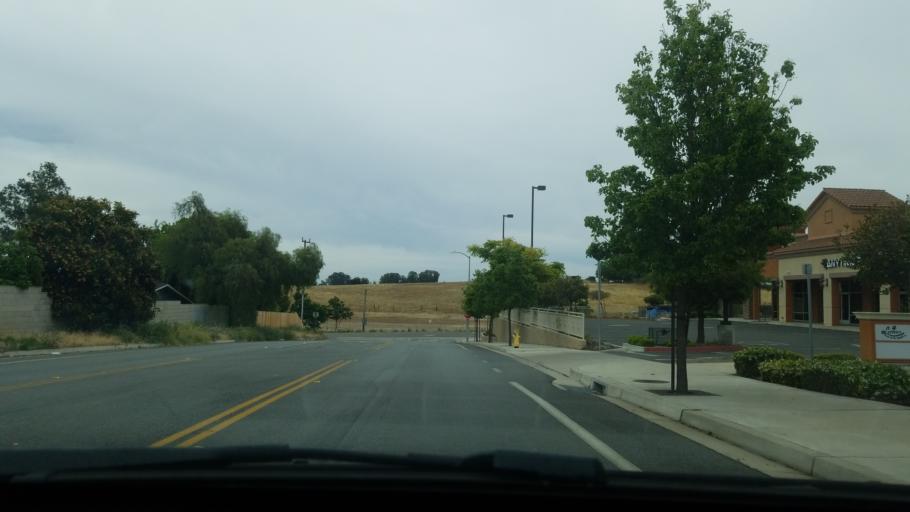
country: US
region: California
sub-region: San Luis Obispo County
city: Nipomo
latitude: 35.0343
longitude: -120.4857
